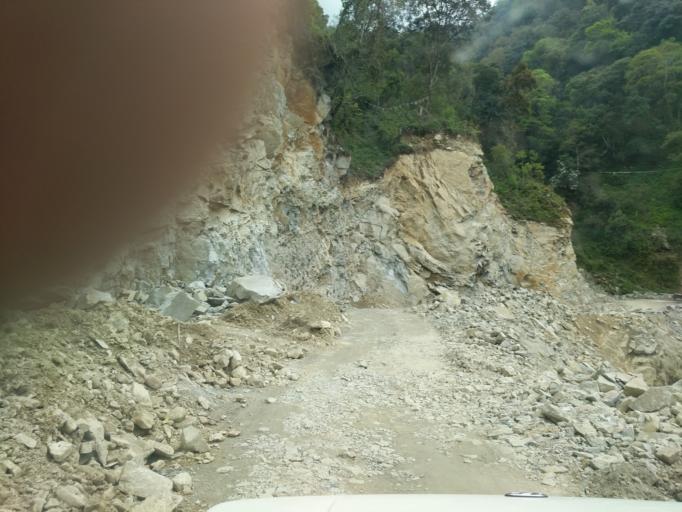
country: BT
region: Mongar
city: Mongar
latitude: 27.2679
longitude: 91.3000
